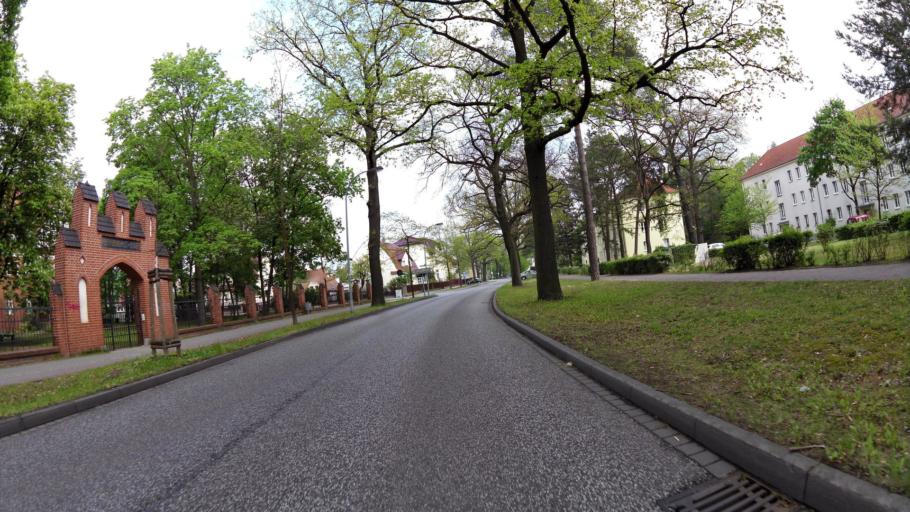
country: DE
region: Brandenburg
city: Konigs Wusterhausen
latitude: 52.2911
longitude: 13.6186
